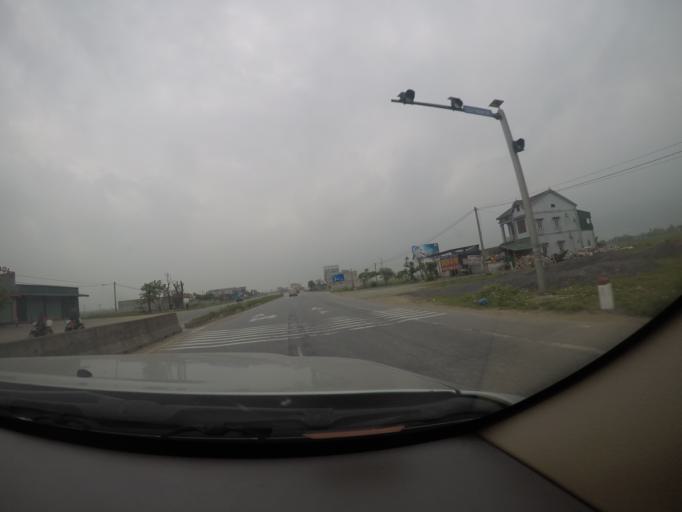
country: VN
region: Ha Tinh
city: Ky Anh
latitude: 18.1108
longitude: 106.2667
